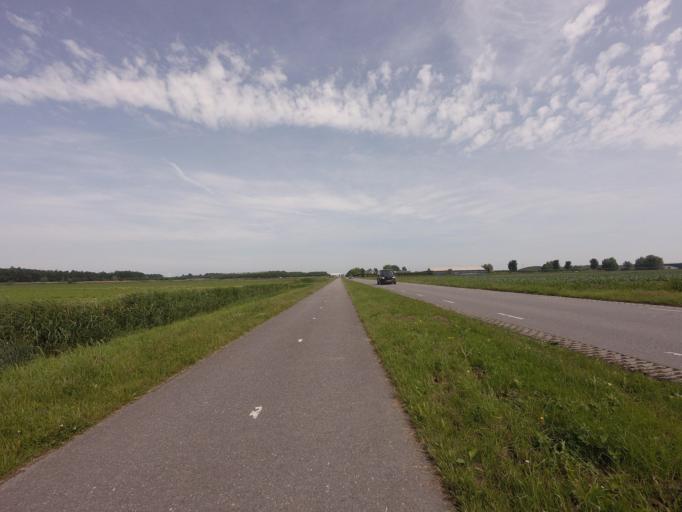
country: NL
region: North Holland
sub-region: Gemeente Enkhuizen
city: Enkhuizen
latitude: 52.7083
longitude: 5.2079
